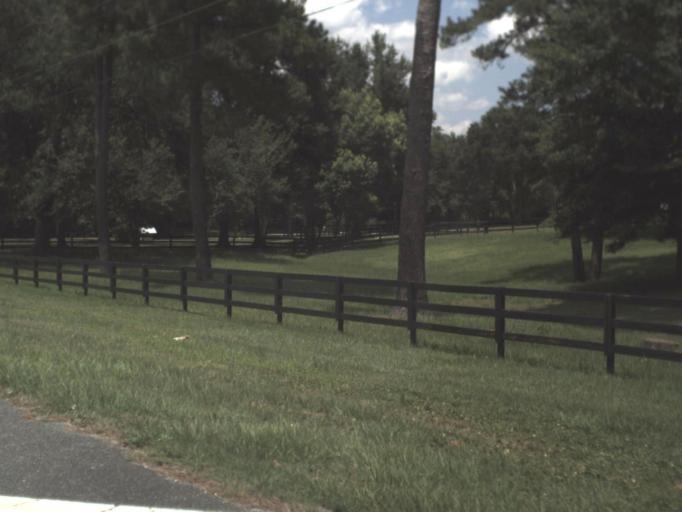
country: US
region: Florida
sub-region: Baker County
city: Macclenny
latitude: 30.3483
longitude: -82.1277
